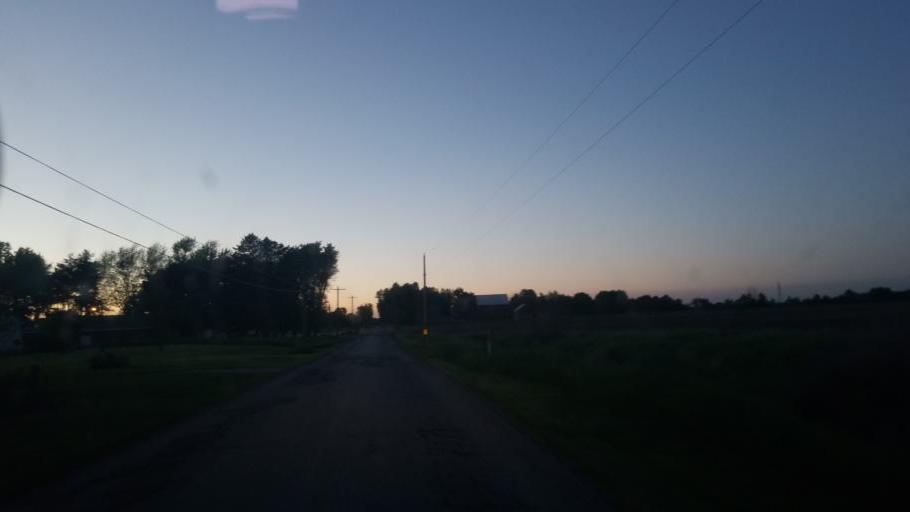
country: US
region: Indiana
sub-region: Marshall County
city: Bremen
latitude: 41.4565
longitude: -86.1176
